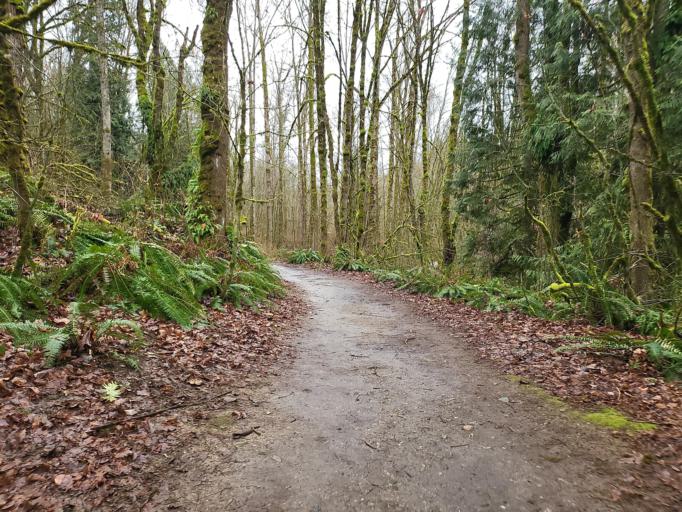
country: US
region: Washington
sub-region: King County
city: Newcastle
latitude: 47.5338
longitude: -122.1282
